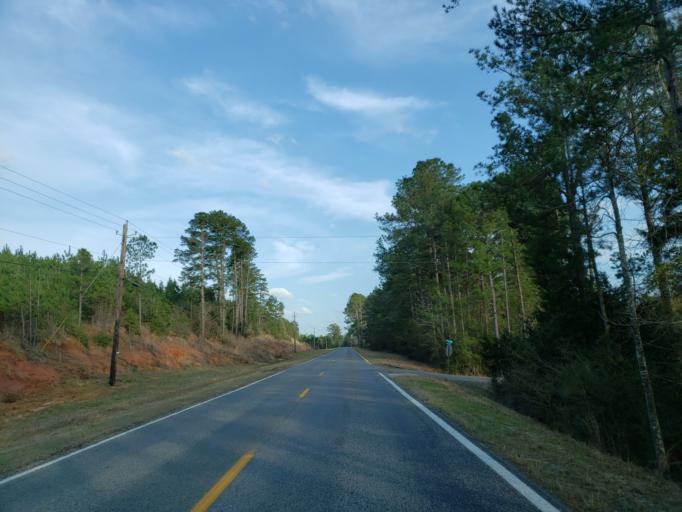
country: US
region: Mississippi
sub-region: Clarke County
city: Stonewall
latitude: 32.1761
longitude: -88.7938
